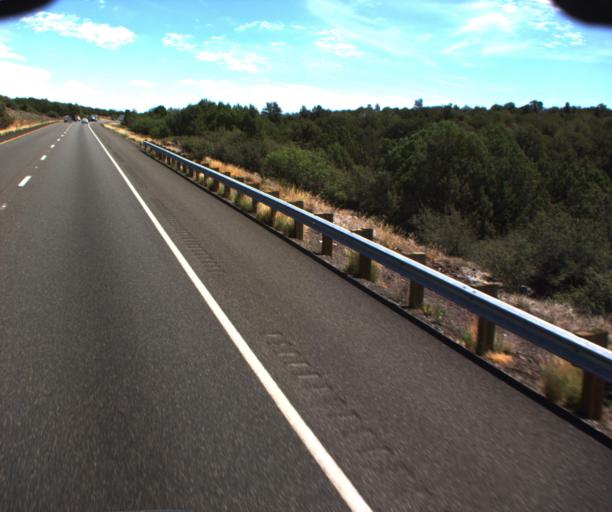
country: US
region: Arizona
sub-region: Yavapai County
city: Big Park
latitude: 34.7283
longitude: -111.7081
